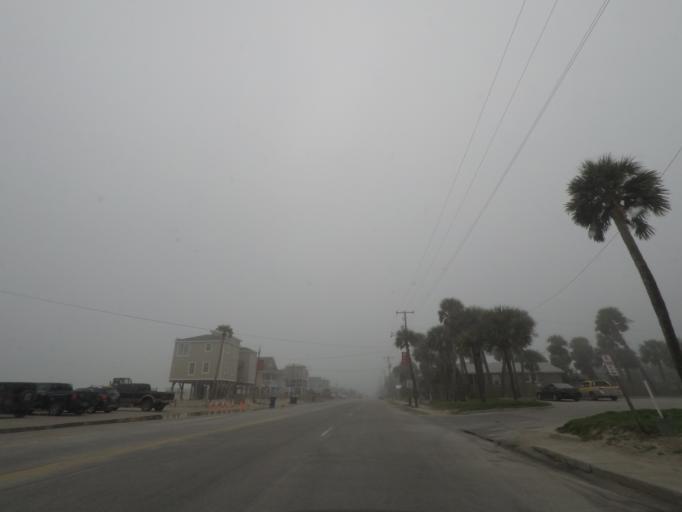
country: US
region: South Carolina
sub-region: Charleston County
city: Seabrook Island
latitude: 32.5032
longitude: -80.2968
